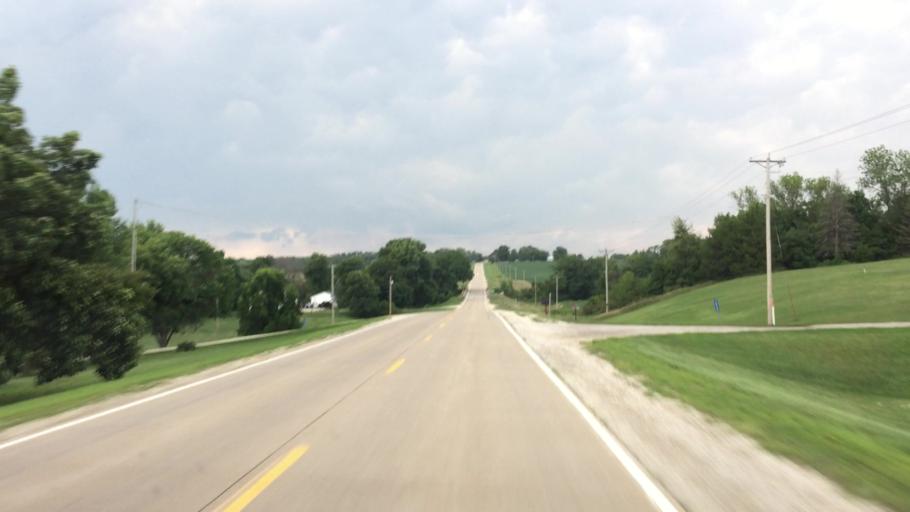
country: US
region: Iowa
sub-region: Lee County
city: Fort Madison
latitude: 40.7207
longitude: -91.3298
